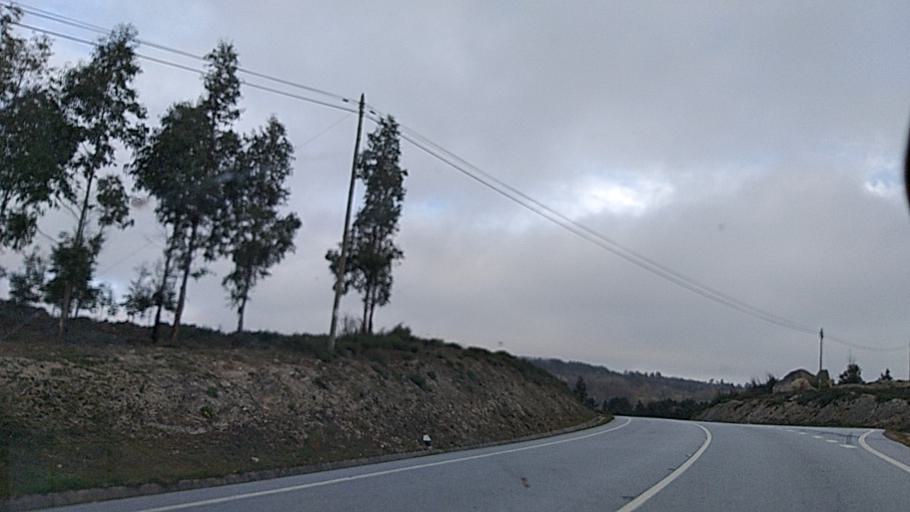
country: PT
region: Guarda
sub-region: Fornos de Algodres
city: Fornos de Algodres
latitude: 40.6674
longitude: -7.4748
